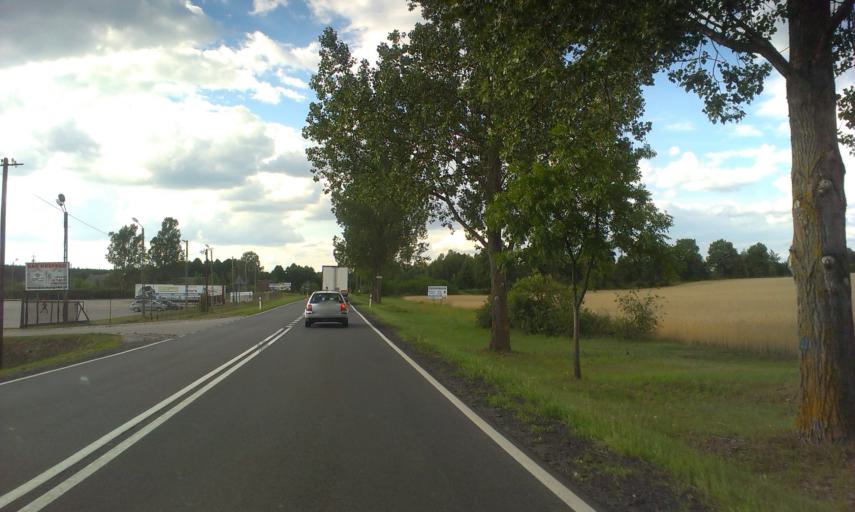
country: PL
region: Greater Poland Voivodeship
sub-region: Powiat zlotowski
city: Tarnowka
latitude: 53.2605
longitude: 16.7832
